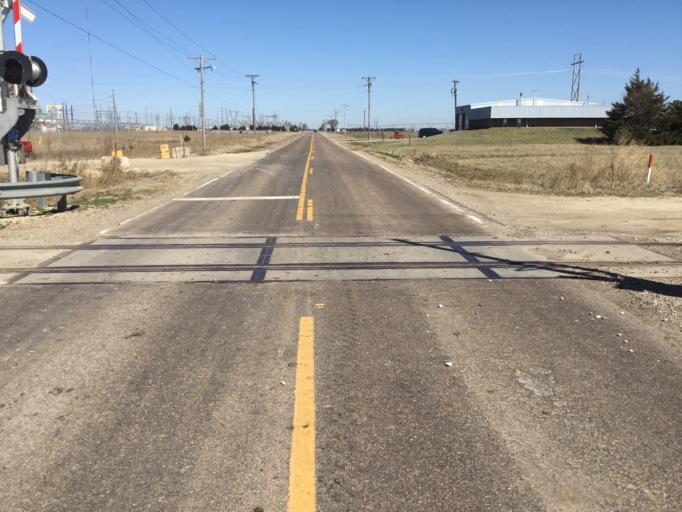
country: US
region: Kansas
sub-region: Sedgwick County
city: Colwich
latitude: 37.7848
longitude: -97.5180
